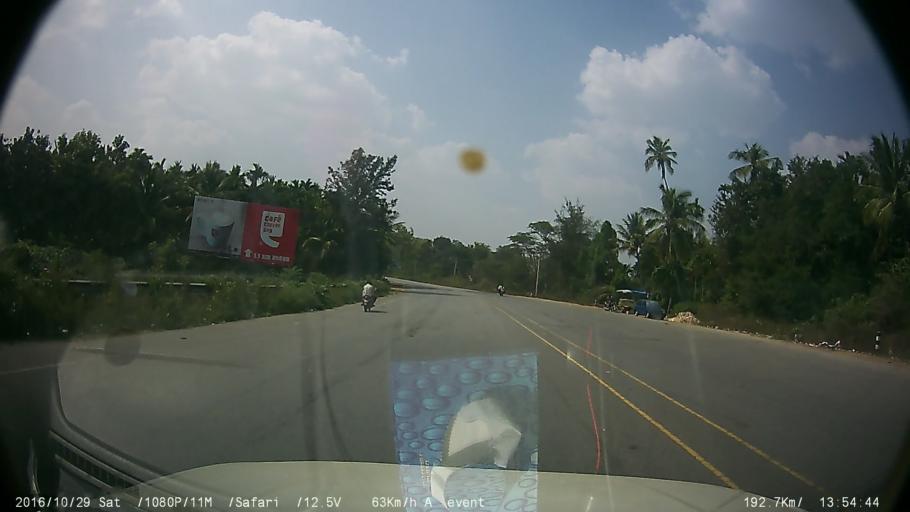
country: IN
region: Karnataka
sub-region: Mysore
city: Piriyapatna
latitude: 12.3375
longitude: 76.1764
